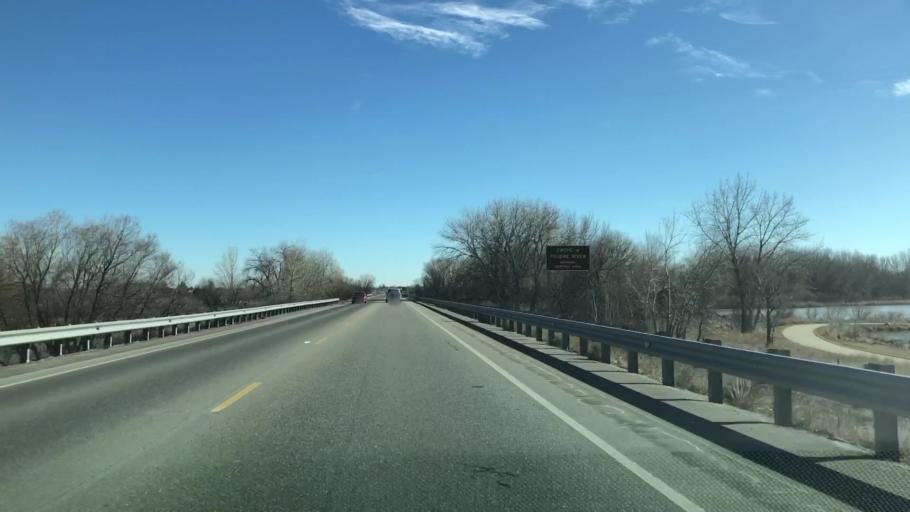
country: US
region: Colorado
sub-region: Weld County
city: Windsor
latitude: 40.4792
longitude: -104.9570
